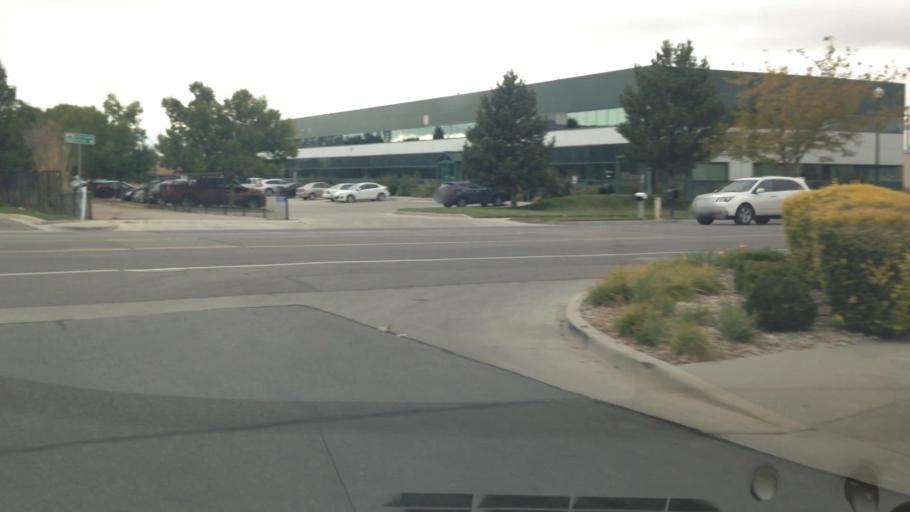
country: US
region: Utah
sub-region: Salt Lake County
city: Sandy City
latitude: 40.5761
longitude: -111.9052
